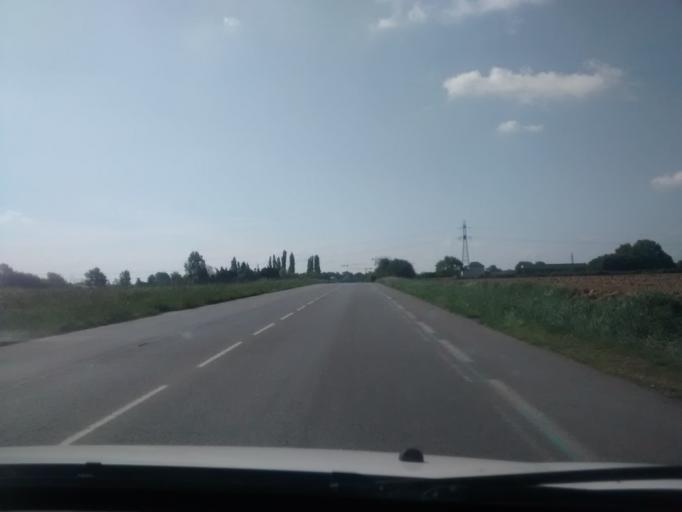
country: FR
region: Brittany
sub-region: Departement d'Ille-et-Vilaine
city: Montgermont
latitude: 48.1467
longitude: -1.7033
